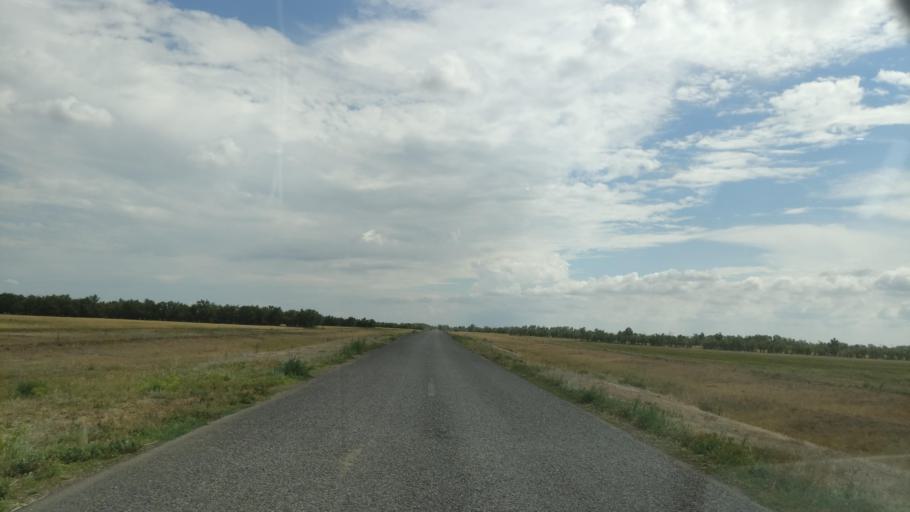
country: KZ
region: Pavlodar
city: Pavlodar
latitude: 52.6367
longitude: 76.9734
